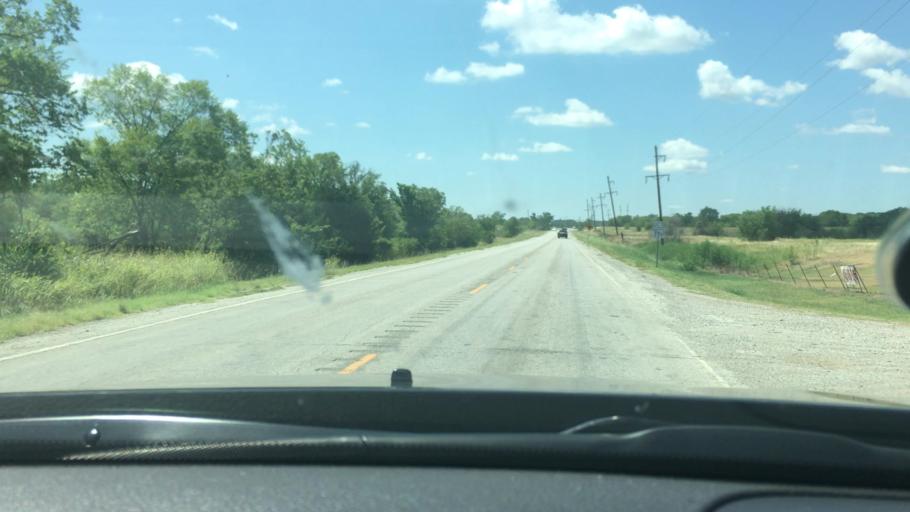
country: US
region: Oklahoma
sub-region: Carter County
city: Ardmore
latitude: 34.0773
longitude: -97.1429
